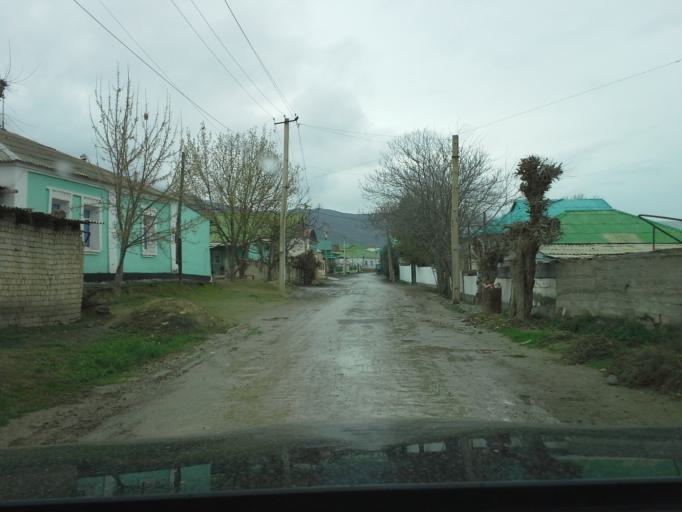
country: TM
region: Ahal
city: Abadan
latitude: 37.9613
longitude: 58.2081
